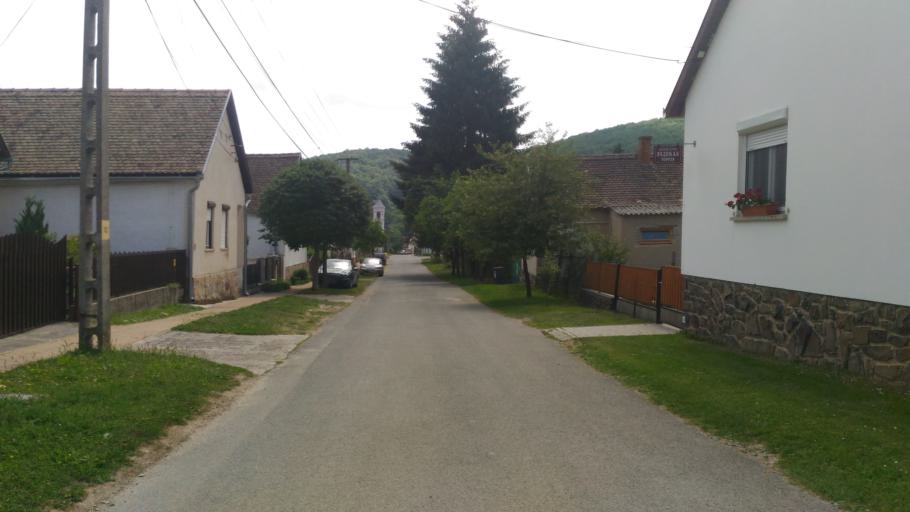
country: HU
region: Baranya
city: Mecseknadasd
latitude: 46.2216
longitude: 18.4088
